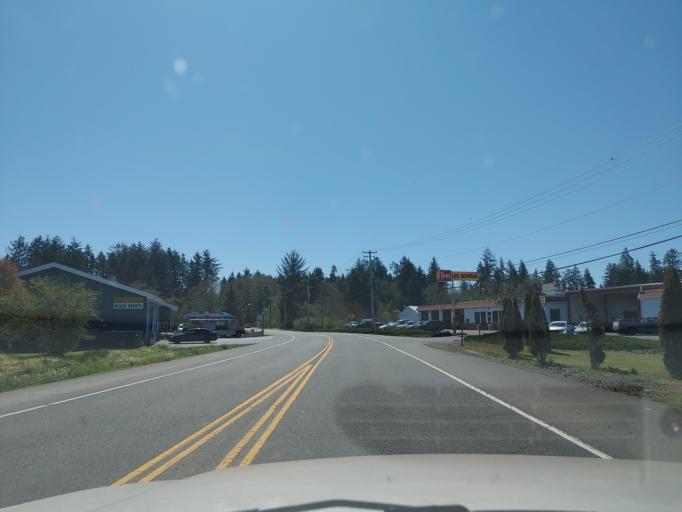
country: US
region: Oregon
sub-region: Clatsop County
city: Warrenton
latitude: 46.1559
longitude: -123.9047
